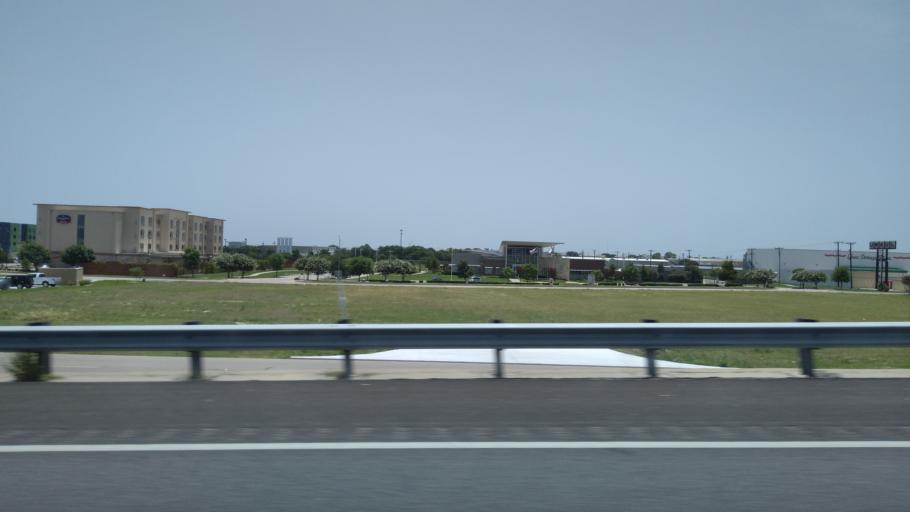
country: US
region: Texas
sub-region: McLennan County
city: Woodway
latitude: 31.5051
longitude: -97.2027
